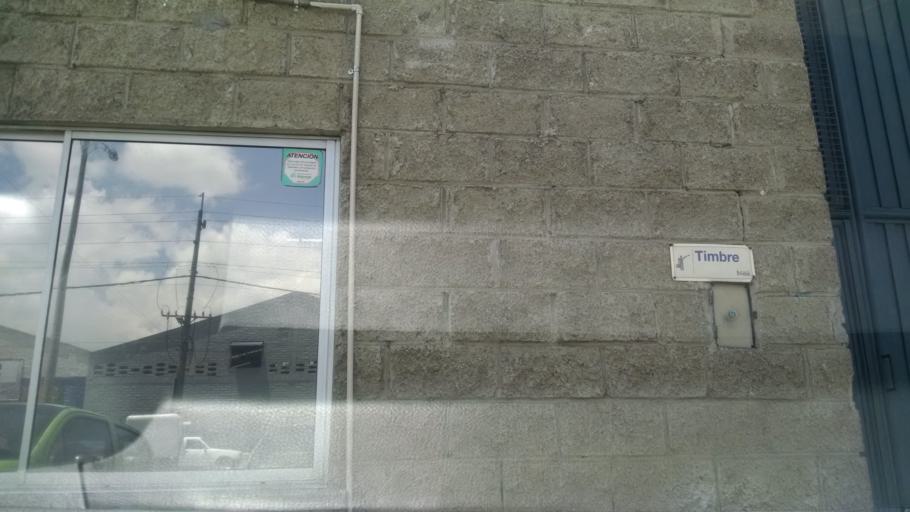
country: CO
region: Antioquia
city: Sabaneta
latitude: 6.1615
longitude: -75.6141
